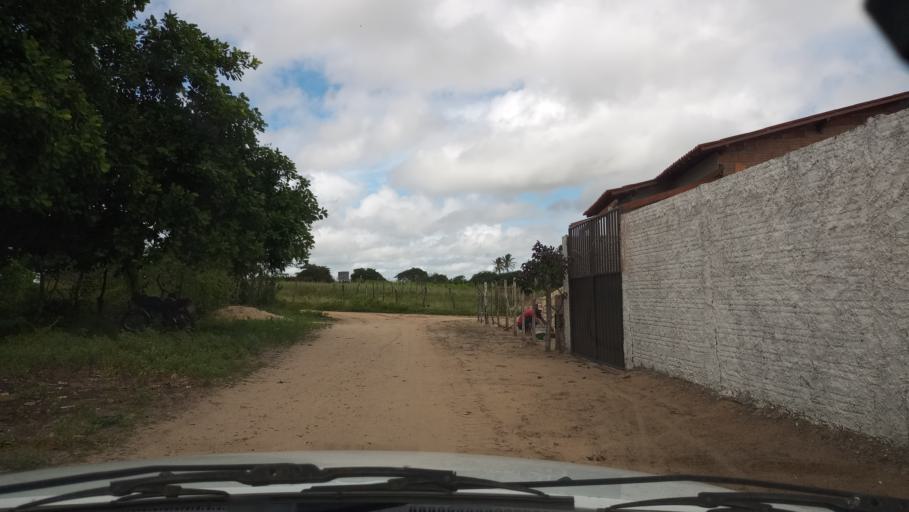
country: BR
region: Rio Grande do Norte
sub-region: Brejinho
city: Brejinho
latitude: -6.1540
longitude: -35.4372
